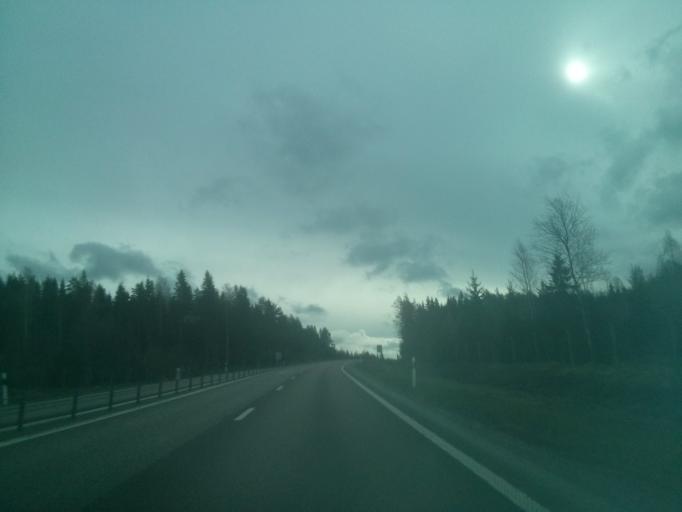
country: SE
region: Vaesternorrland
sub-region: Timra Kommun
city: Soraker
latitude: 62.5338
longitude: 17.5102
